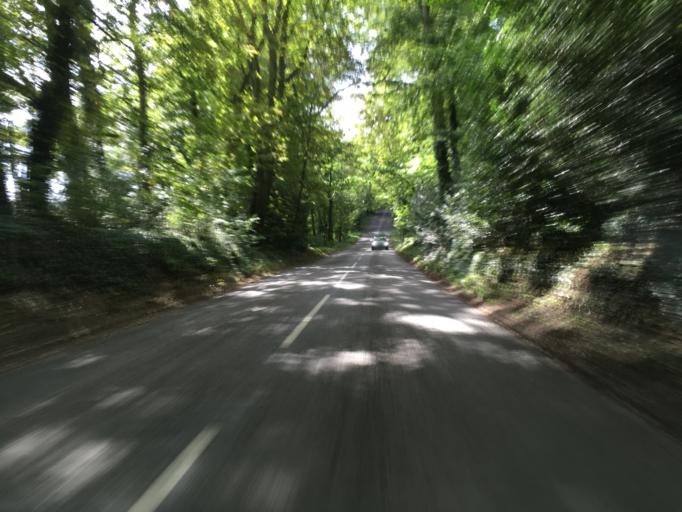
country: GB
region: England
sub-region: Hampshire
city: Overton
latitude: 51.1772
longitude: -1.2492
